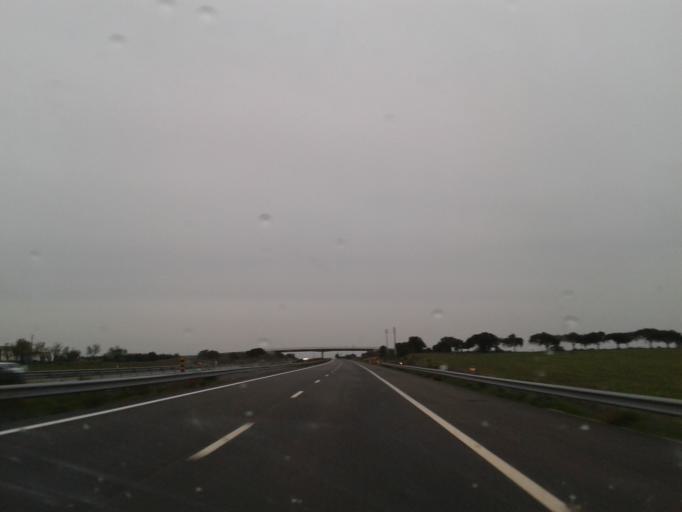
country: PT
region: Beja
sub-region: Aljustrel
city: Aljustrel
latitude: 38.0243
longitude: -8.2856
